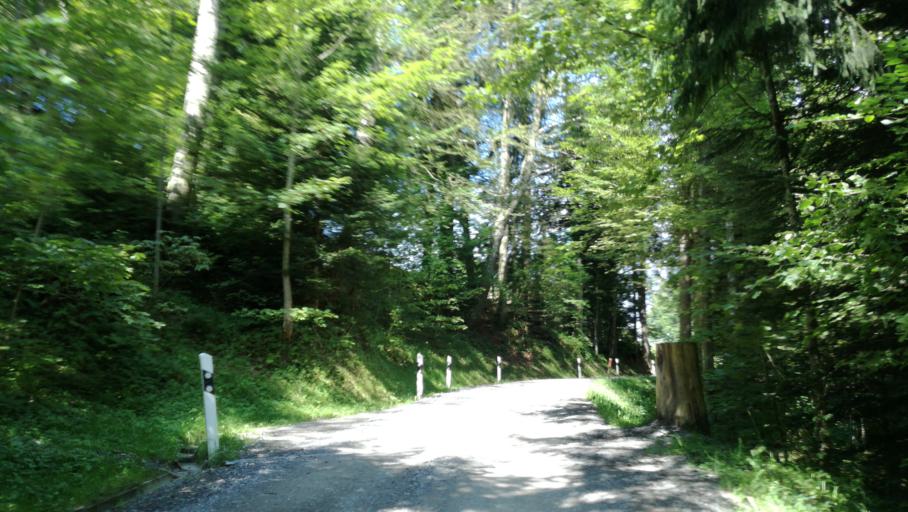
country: CH
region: Zug
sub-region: Zug
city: Unterageri
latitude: 47.1460
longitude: 8.5969
